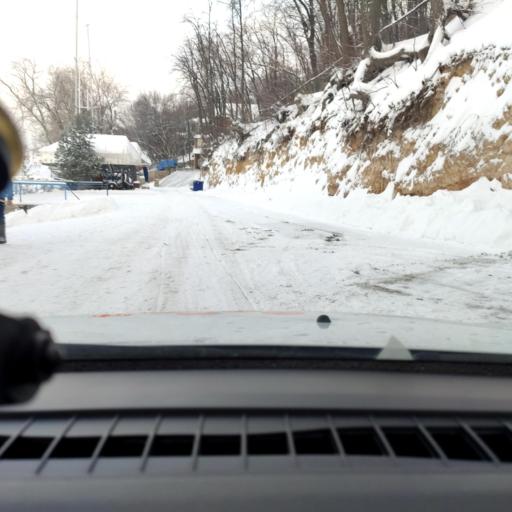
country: RU
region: Samara
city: Samara
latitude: 53.2932
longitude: 50.1925
